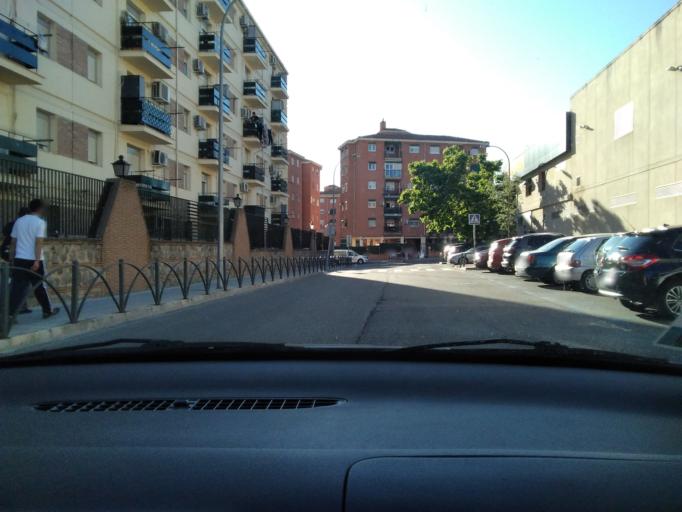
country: ES
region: Castille-La Mancha
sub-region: Province of Toledo
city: Toledo
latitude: 39.8731
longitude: -4.0377
